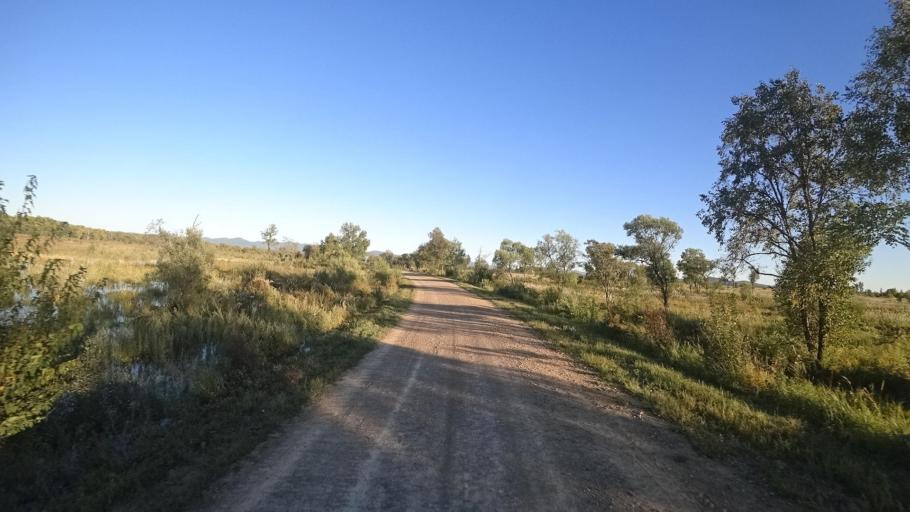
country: RU
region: Primorskiy
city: Kirovskiy
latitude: 44.8155
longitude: 133.6115
